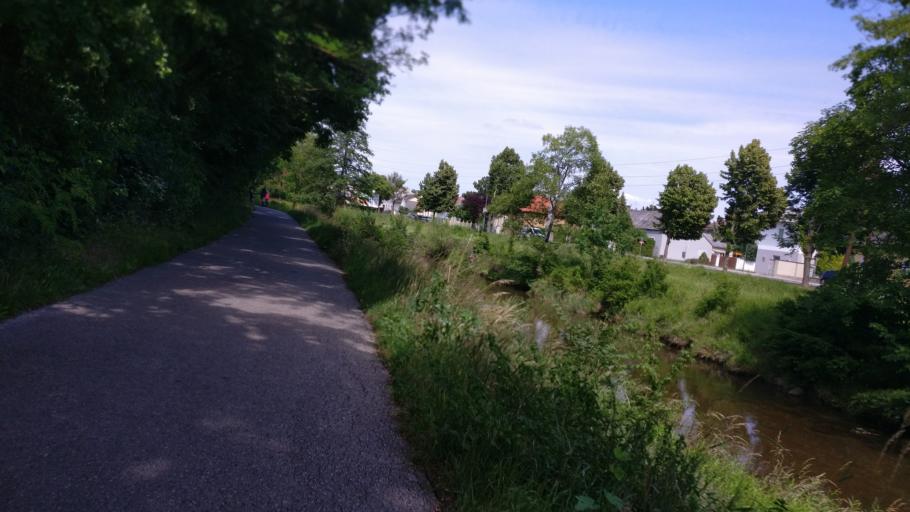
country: AT
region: Lower Austria
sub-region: Politischer Bezirk Baden
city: Oberwaltersdorf
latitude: 47.9718
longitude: 16.3206
